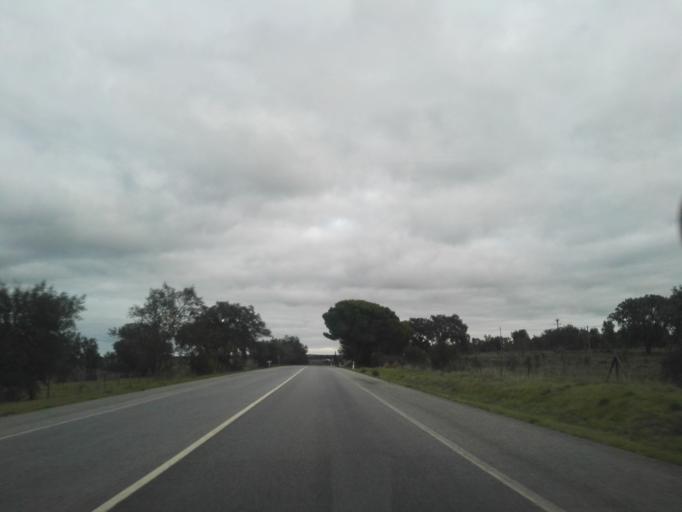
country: PT
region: Evora
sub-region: Montemor-O-Novo
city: Montemor-o-Novo
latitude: 38.6396
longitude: -8.1359
